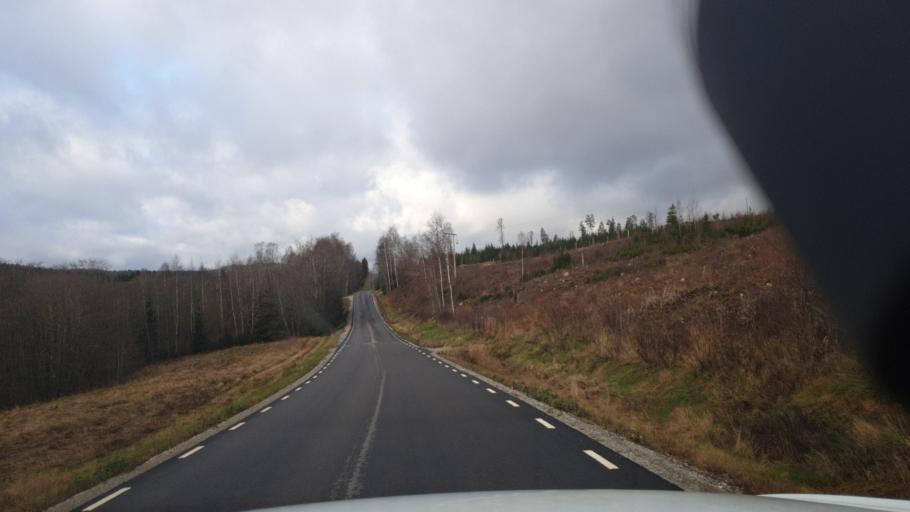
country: SE
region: Vaermland
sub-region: Sunne Kommun
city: Sunne
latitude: 59.6714
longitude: 12.9051
